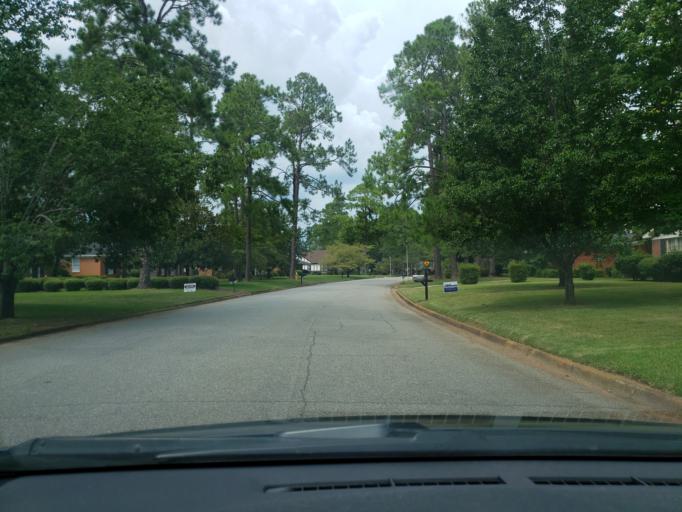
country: US
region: Georgia
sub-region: Dougherty County
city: Albany
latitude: 31.5983
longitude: -84.2066
